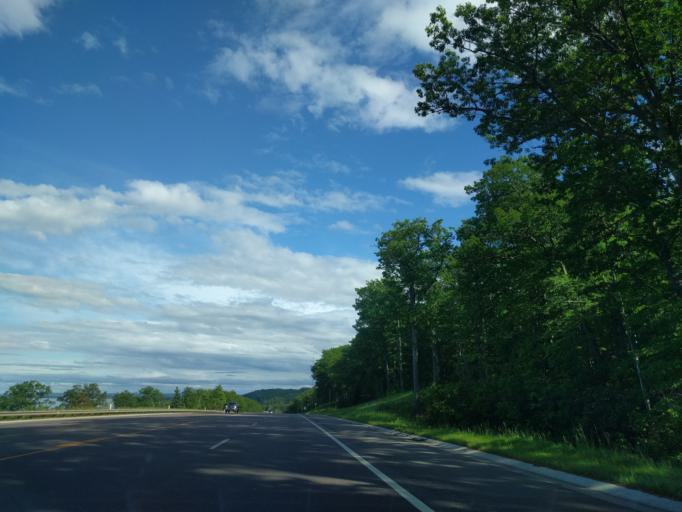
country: US
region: Michigan
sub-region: Marquette County
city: Marquette
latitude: 46.5238
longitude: -87.3920
